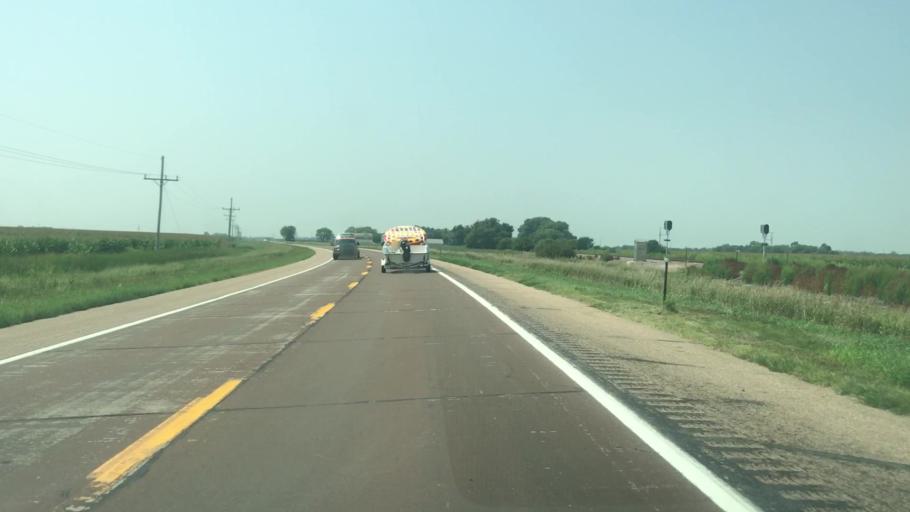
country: US
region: Nebraska
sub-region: Hall County
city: Grand Island
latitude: 40.9670
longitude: -98.4458
